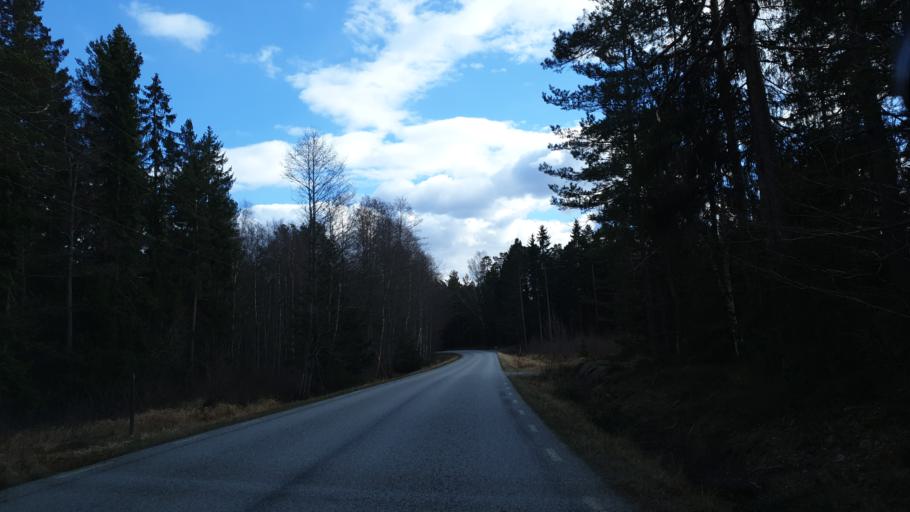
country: SE
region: Stockholm
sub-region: Varmdo Kommun
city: Hemmesta
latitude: 59.2297
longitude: 18.4848
